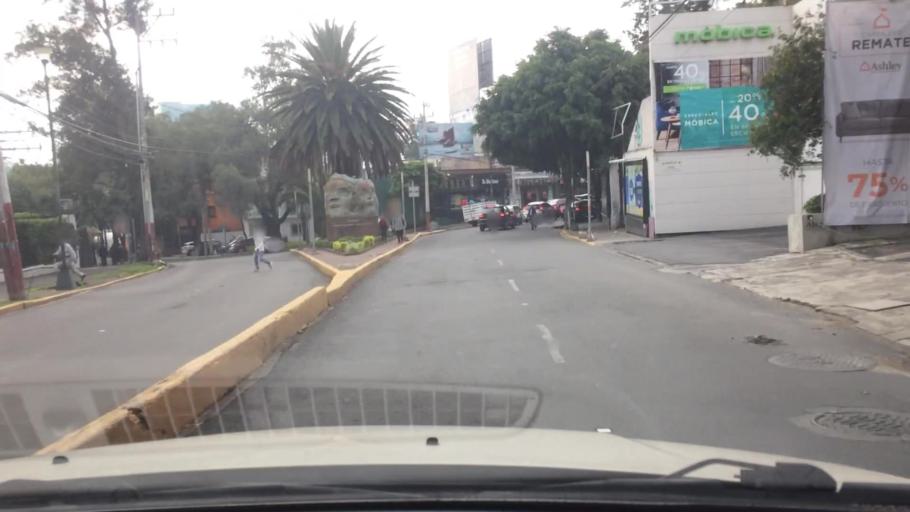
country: MX
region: Mexico City
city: Alvaro Obregon
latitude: 19.3482
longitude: -99.1920
